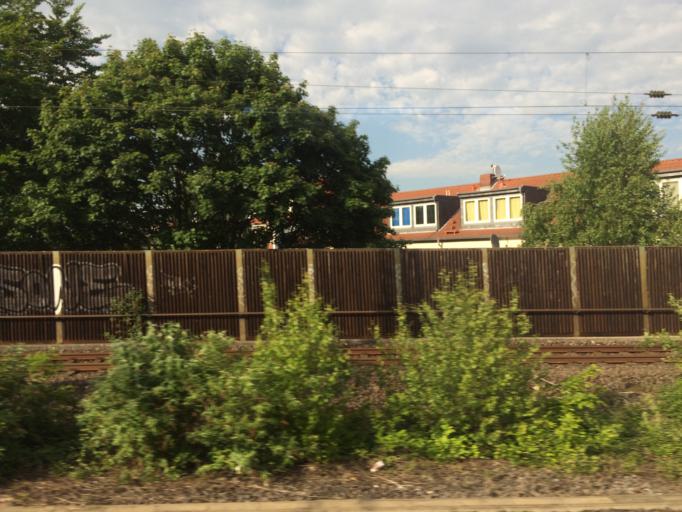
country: DE
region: North Rhine-Westphalia
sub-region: Regierungsbezirk Koln
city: Humboldtkolonie
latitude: 50.9344
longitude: 7.0007
